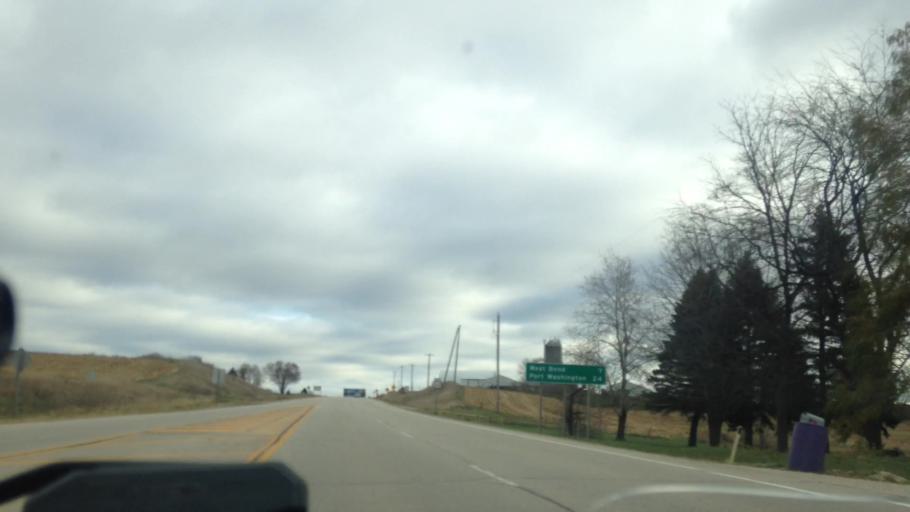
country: US
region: Wisconsin
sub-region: Washington County
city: Slinger
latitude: 43.4250
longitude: -88.3325
